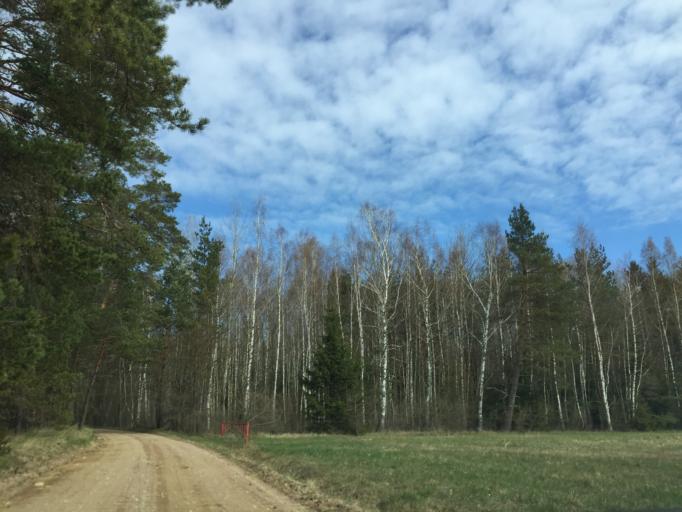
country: LV
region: Salacgrivas
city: Salacgriva
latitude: 57.5964
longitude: 24.3738
